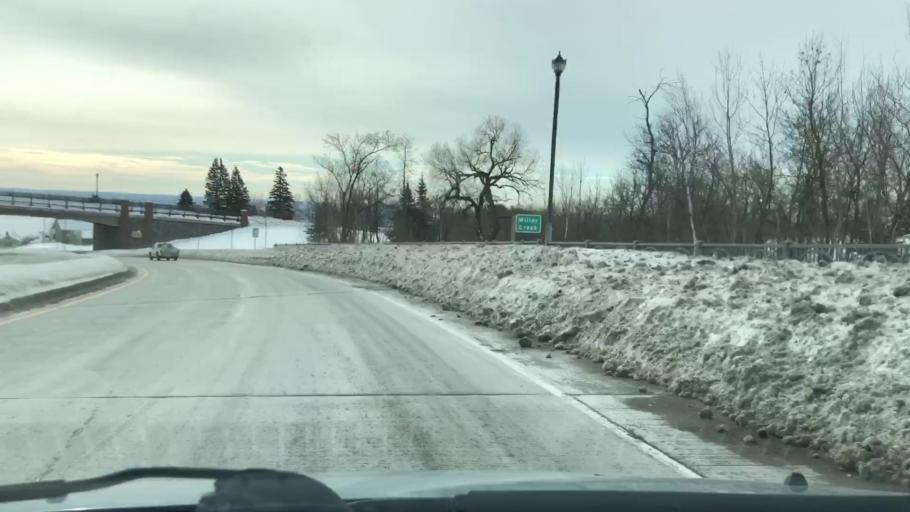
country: US
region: Minnesota
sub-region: Saint Louis County
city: Duluth
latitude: 46.7748
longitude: -92.1431
